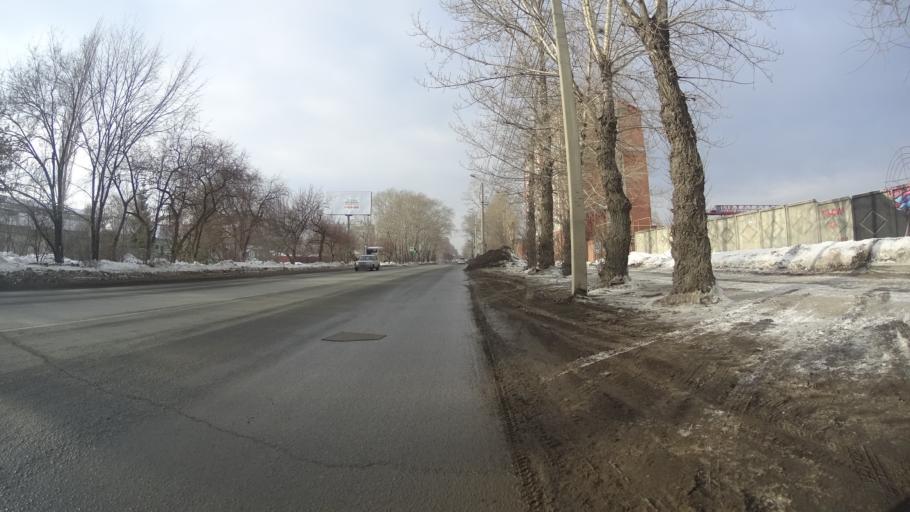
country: RU
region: Chelyabinsk
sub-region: Gorod Chelyabinsk
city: Chelyabinsk
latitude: 55.1210
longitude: 61.3789
